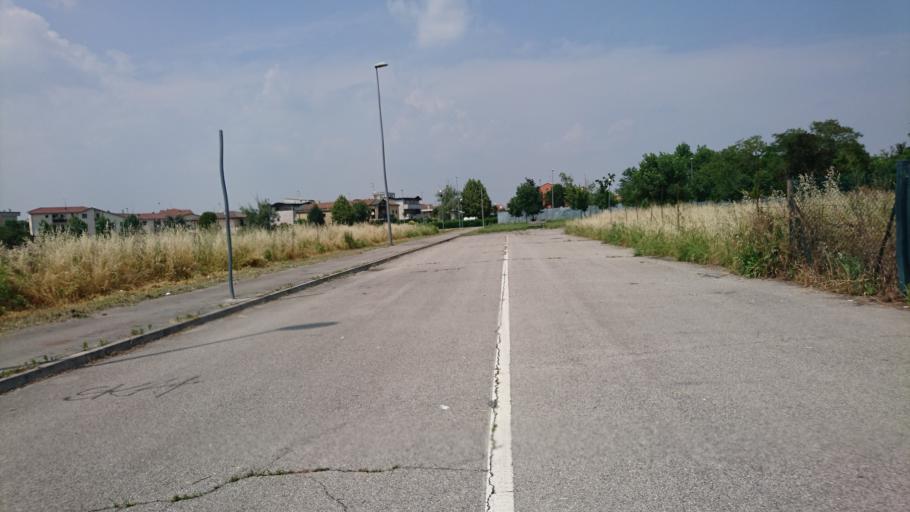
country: IT
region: Veneto
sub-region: Provincia di Padova
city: Masera di Padova
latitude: 45.3145
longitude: 11.8674
